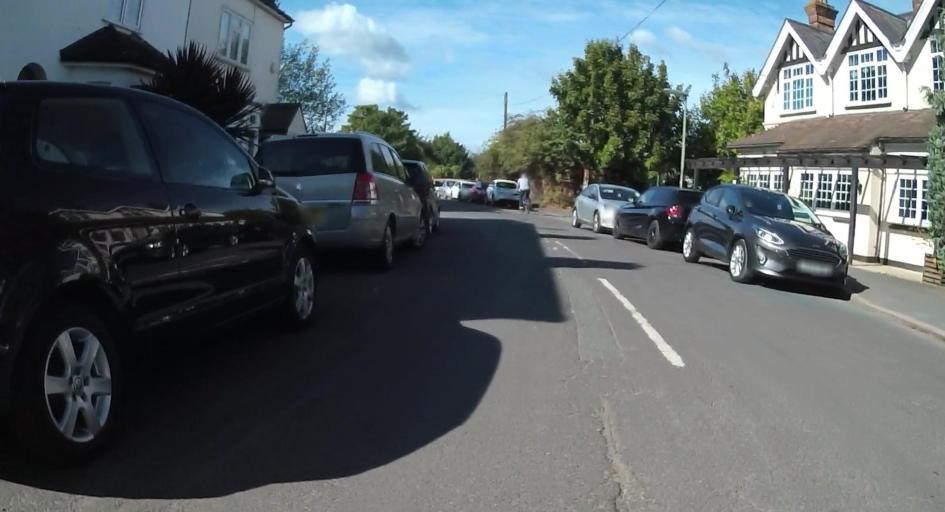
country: GB
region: England
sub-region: Surrey
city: Addlestone
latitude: 51.3814
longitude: -0.4907
